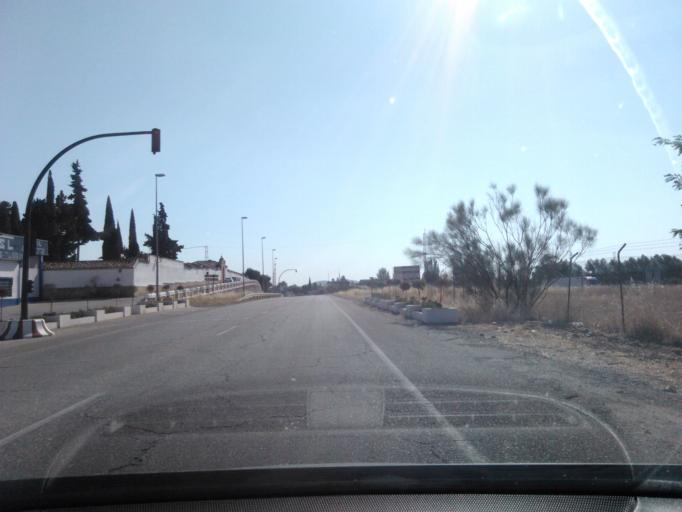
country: ES
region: Andalusia
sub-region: Provincia de Jaen
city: La Carolina
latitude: 38.2791
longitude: -3.6016
